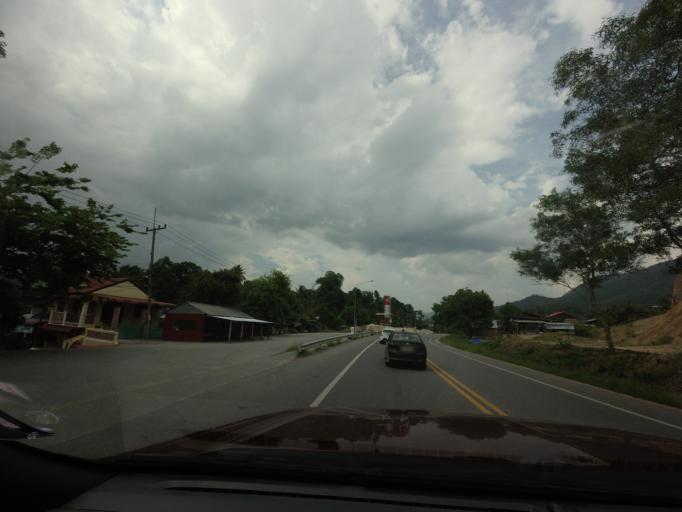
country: TH
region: Yala
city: Ban Nang Sata
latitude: 6.2797
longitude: 101.2909
